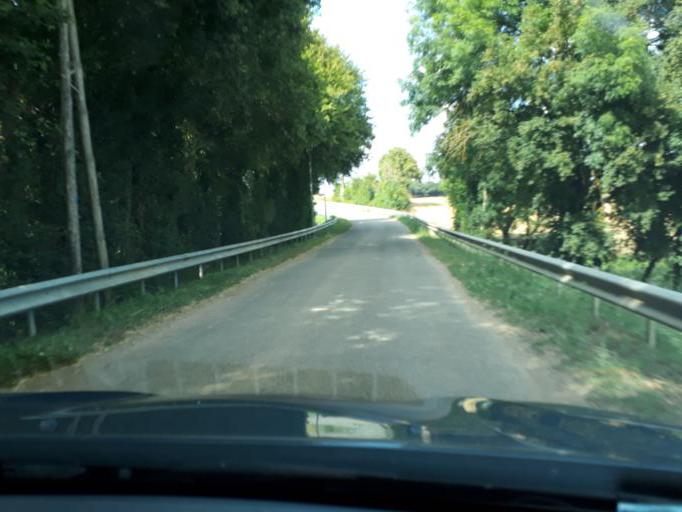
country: FR
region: Centre
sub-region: Departement du Cher
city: Jouet-sur-l'Aubois
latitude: 47.0029
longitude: 2.9134
